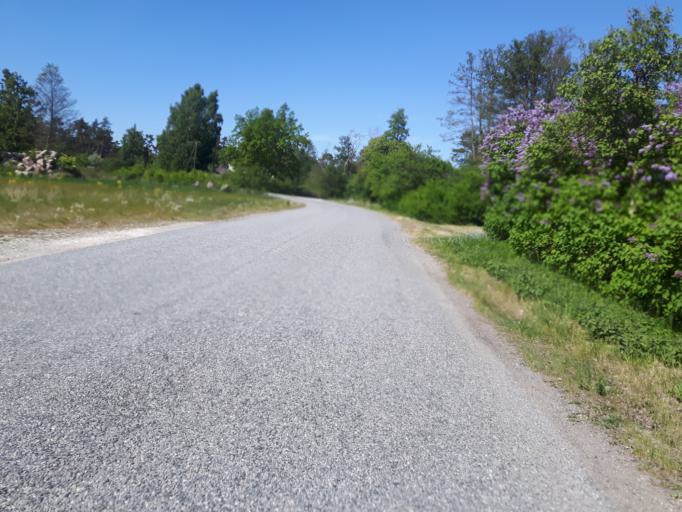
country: EE
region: Laeaene-Virumaa
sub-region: Haljala vald
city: Haljala
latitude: 59.5673
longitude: 26.2995
